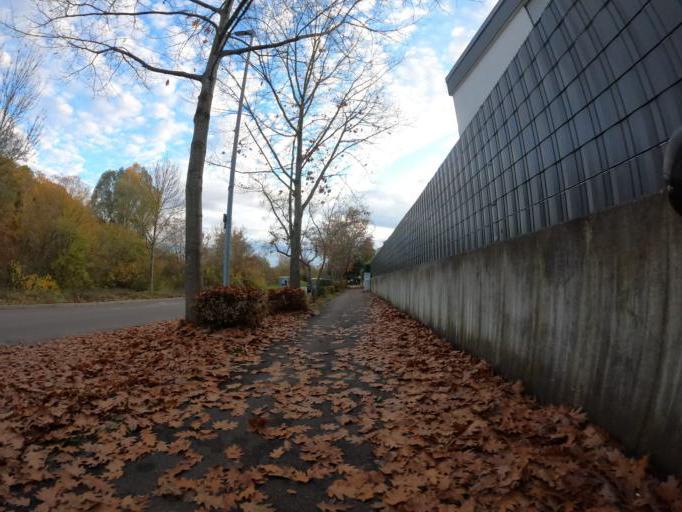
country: DE
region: Baden-Wuerttemberg
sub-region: Regierungsbezirk Stuttgart
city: Magstadt
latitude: 48.7218
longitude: 8.9881
